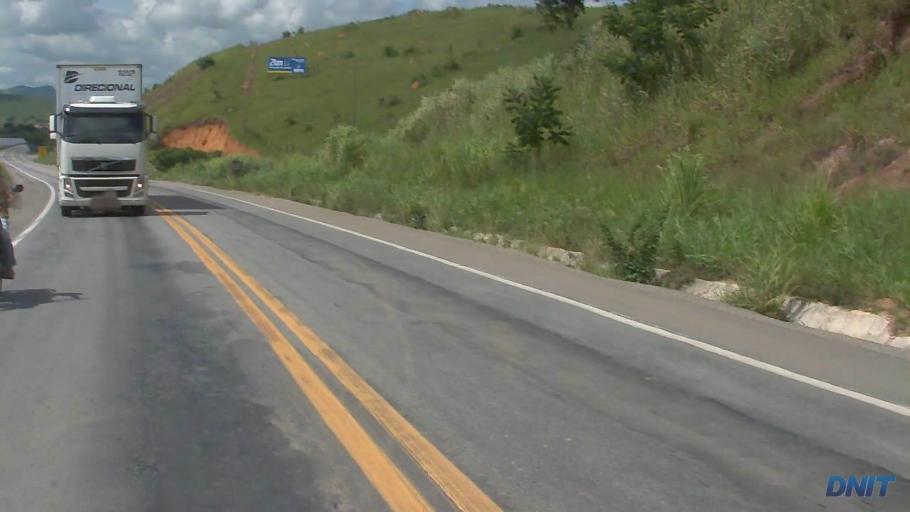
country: BR
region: Minas Gerais
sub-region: Governador Valadares
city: Governador Valadares
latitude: -19.0434
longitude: -42.1509
